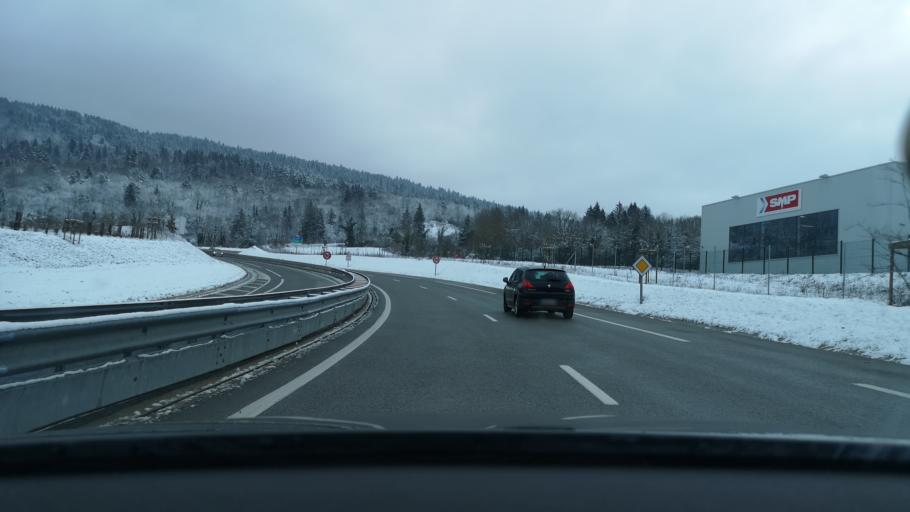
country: FR
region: Rhone-Alpes
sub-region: Departement de l'Ain
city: Dortan
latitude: 46.3242
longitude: 5.6712
